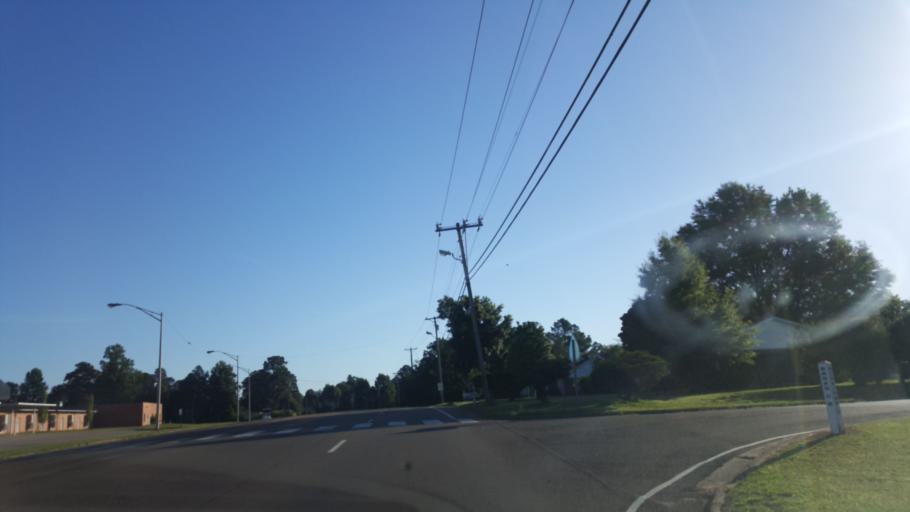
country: US
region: Tennessee
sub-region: Henderson County
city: Lexington
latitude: 35.6578
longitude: -88.3861
